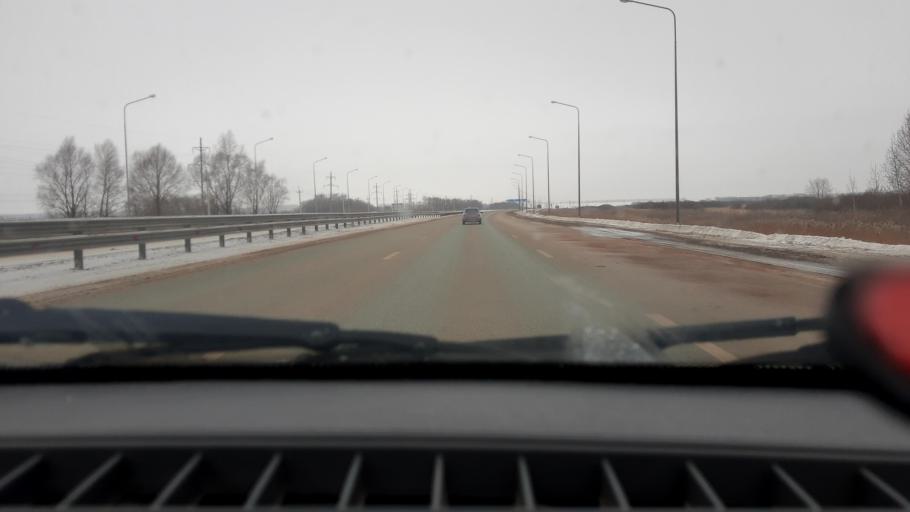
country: RU
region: Bashkortostan
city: Asanovo
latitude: 54.9055
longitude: 55.6153
